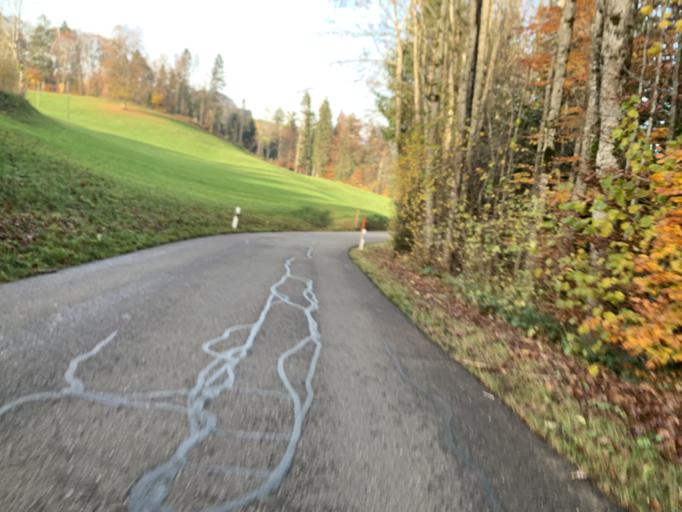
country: CH
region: Zurich
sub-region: Bezirk Hinwil
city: Wald
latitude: 47.3085
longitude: 8.9070
